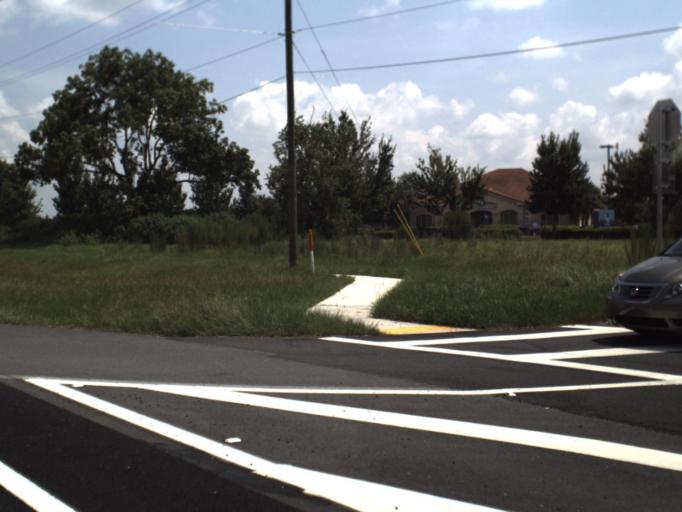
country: US
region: Florida
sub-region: Hillsborough County
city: Lutz
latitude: 28.1739
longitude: -82.4728
